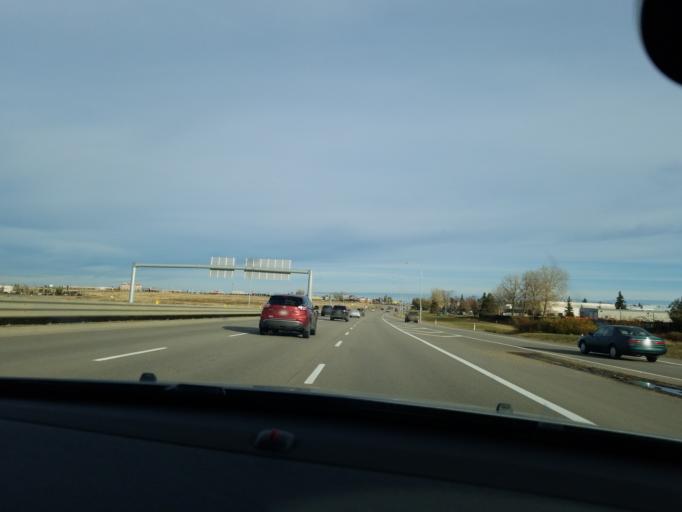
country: CA
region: Alberta
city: Sherwood Park
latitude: 53.5410
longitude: -113.3330
